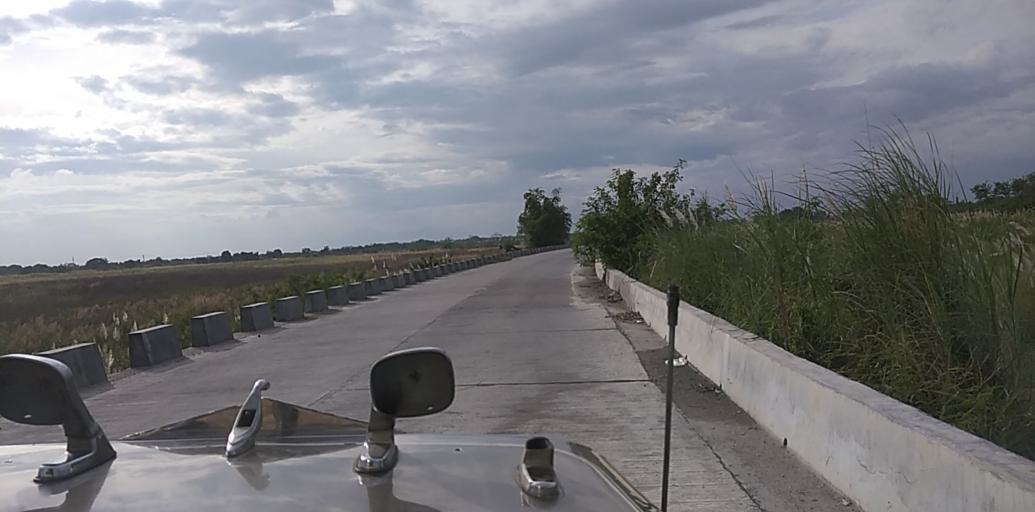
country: PH
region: Central Luzon
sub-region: Province of Pampanga
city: Minalin
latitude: 14.9669
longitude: 120.6687
